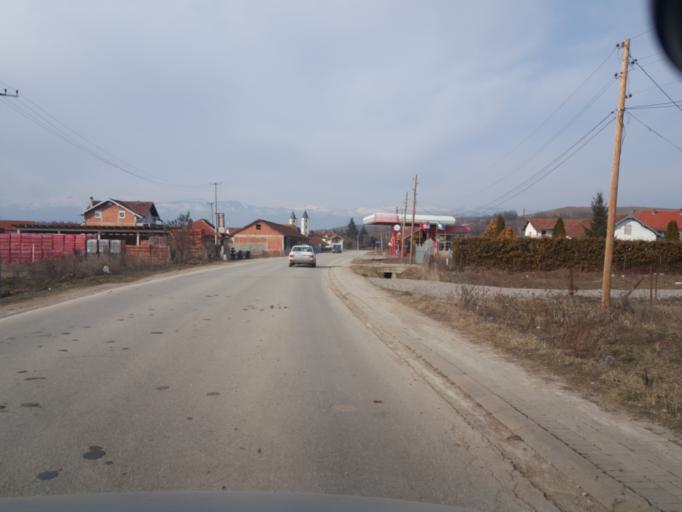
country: XK
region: Pec
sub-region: Komuna e Klines
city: Klina
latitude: 42.6565
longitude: 20.5437
